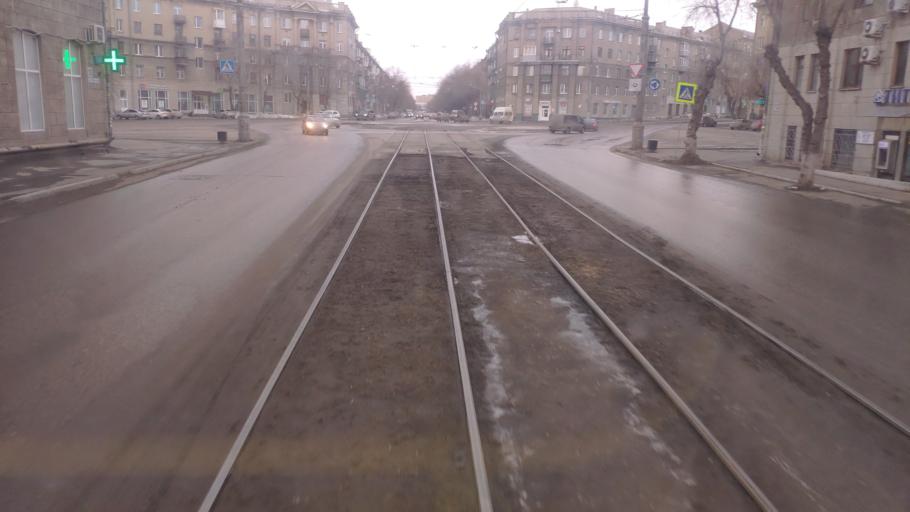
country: RU
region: Chelyabinsk
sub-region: Gorod Magnitogorsk
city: Magnitogorsk
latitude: 53.4184
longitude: 58.9967
